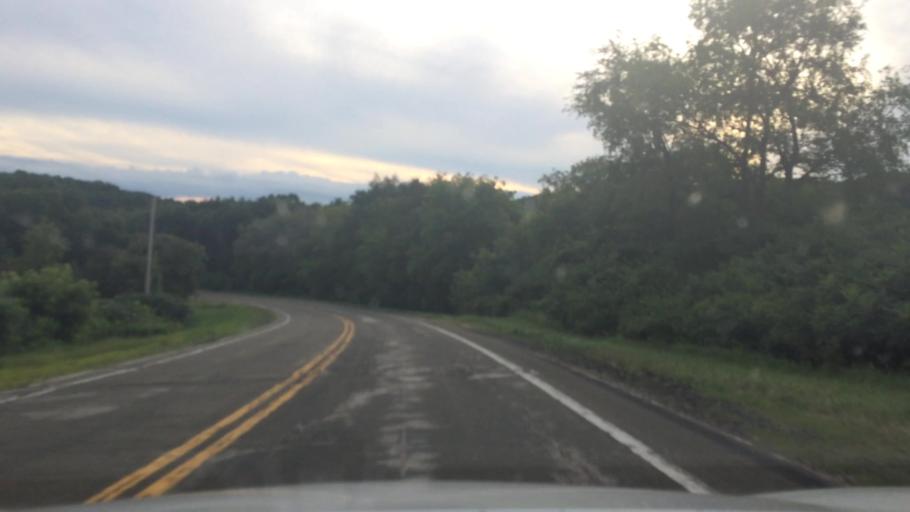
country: US
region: Wisconsin
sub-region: Columbia County
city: Lodi
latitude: 43.3230
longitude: -89.4984
